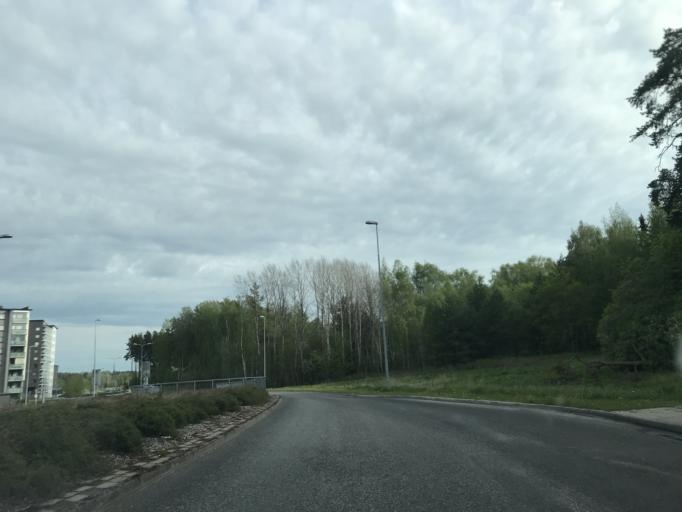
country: FI
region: Varsinais-Suomi
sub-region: Turku
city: Kaarina
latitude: 60.4295
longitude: 22.3191
